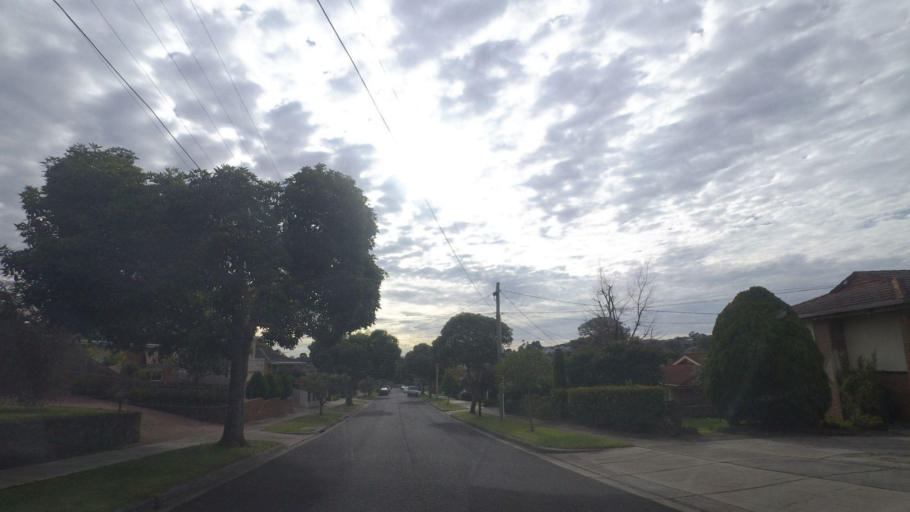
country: AU
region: Victoria
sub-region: Manningham
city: Bulleen
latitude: -37.7650
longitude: 145.0998
